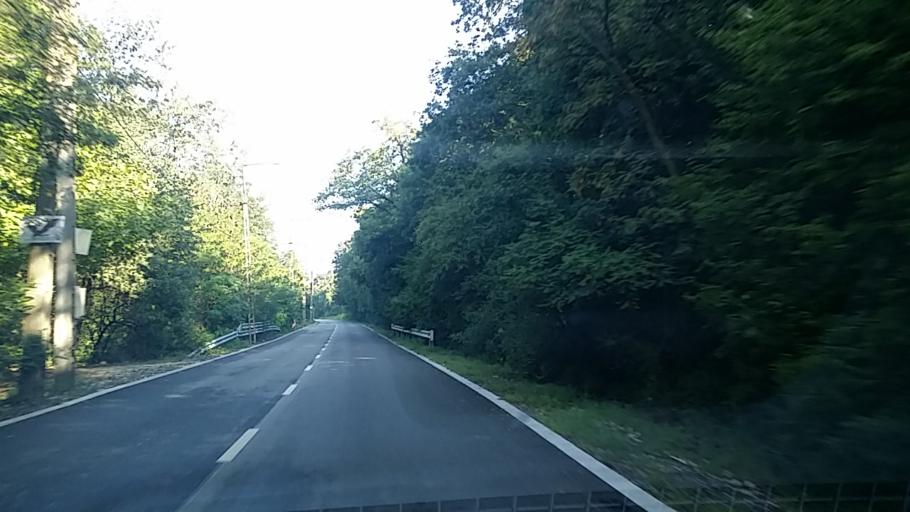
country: HU
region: Komarom-Esztergom
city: Tatabanya
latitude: 47.5823
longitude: 18.4151
